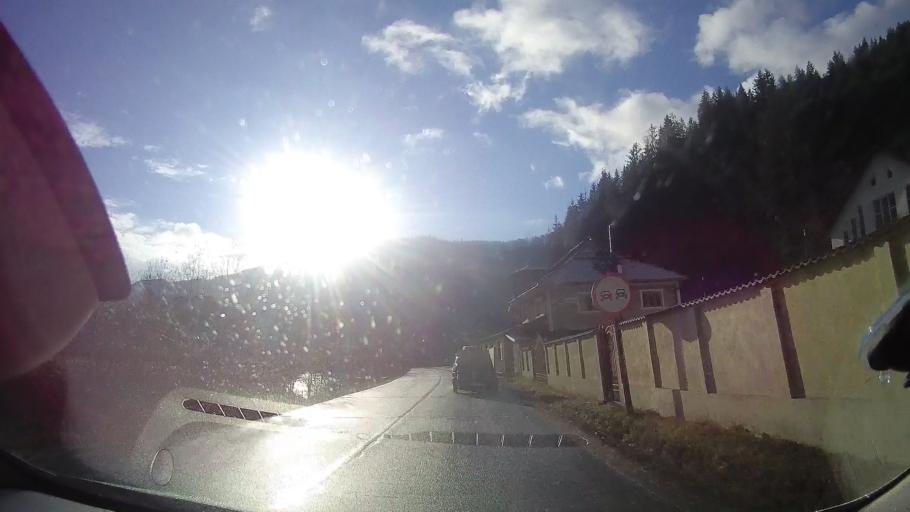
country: RO
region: Alba
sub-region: Comuna Vadu Motilor
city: Vadu Motilor
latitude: 46.3979
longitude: 22.9625
